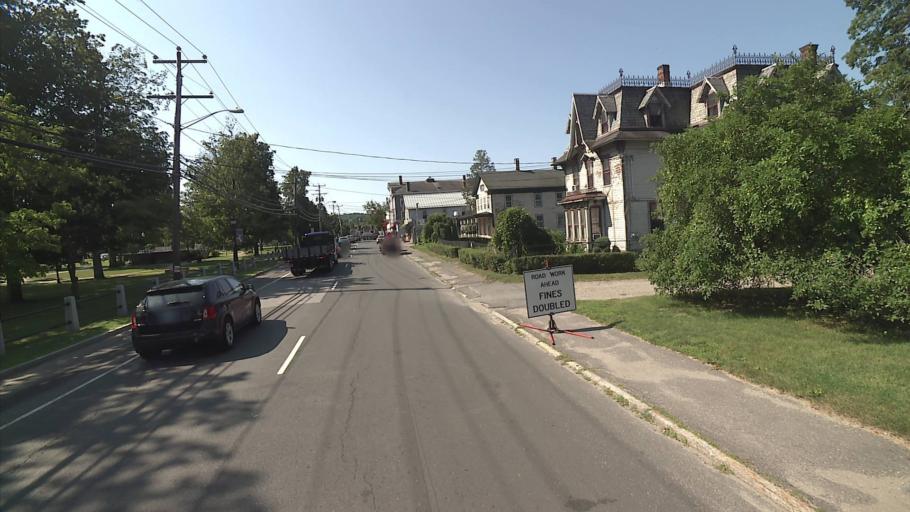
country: US
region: Connecticut
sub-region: Litchfield County
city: Winsted
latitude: 41.9226
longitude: -73.0603
